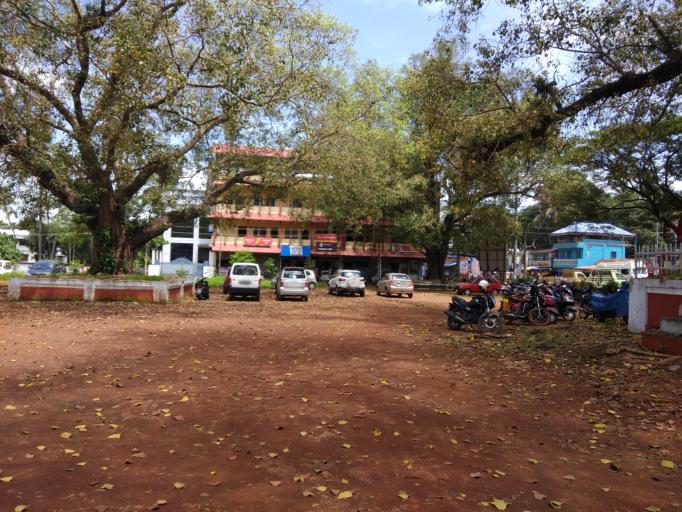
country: IN
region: Kerala
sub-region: Thrissur District
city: Trichur
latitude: 10.5526
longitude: 76.1744
